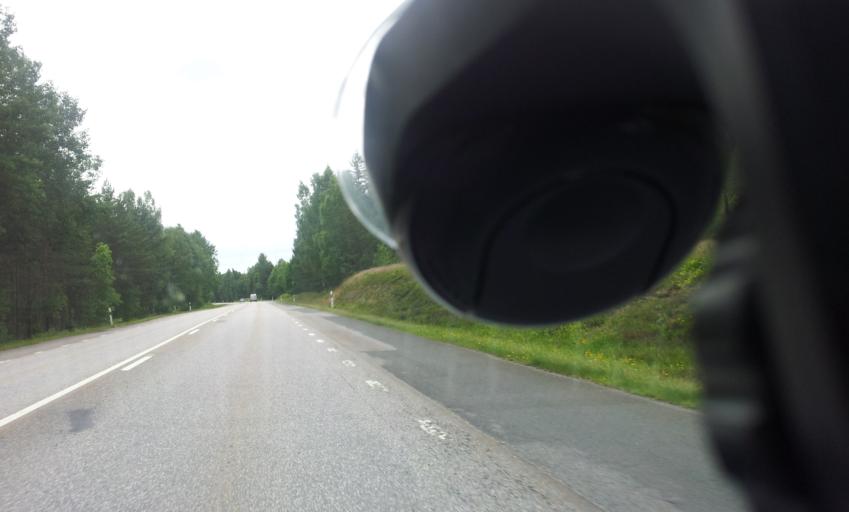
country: SE
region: Kalmar
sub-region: Vasterviks Kommun
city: Ankarsrum
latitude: 57.6968
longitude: 16.4414
